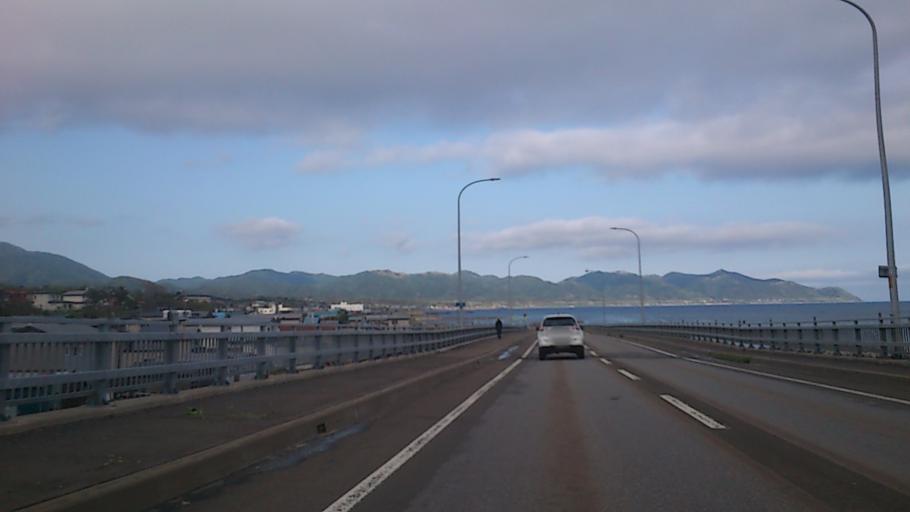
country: JP
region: Aomori
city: Shimokizukuri
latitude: 41.4246
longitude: 140.0924
